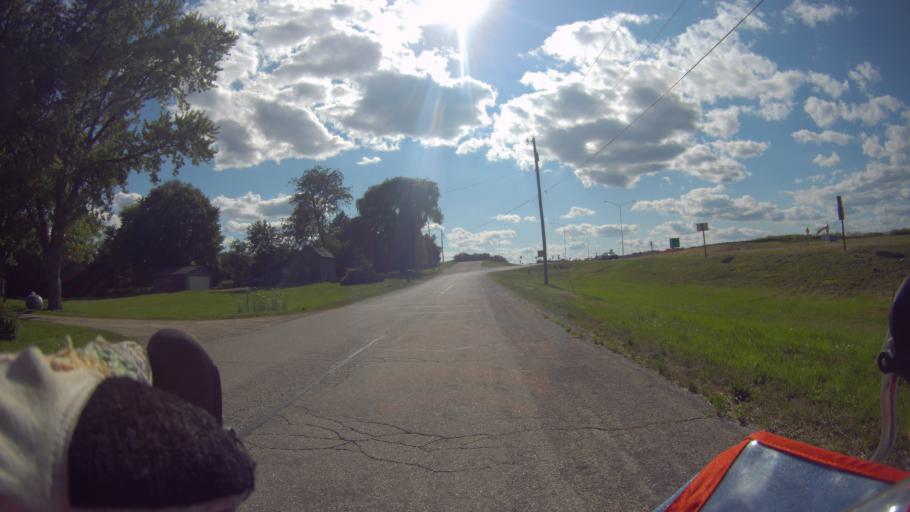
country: US
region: Wisconsin
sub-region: Dane County
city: Stoughton
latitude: 42.9178
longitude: -89.2497
